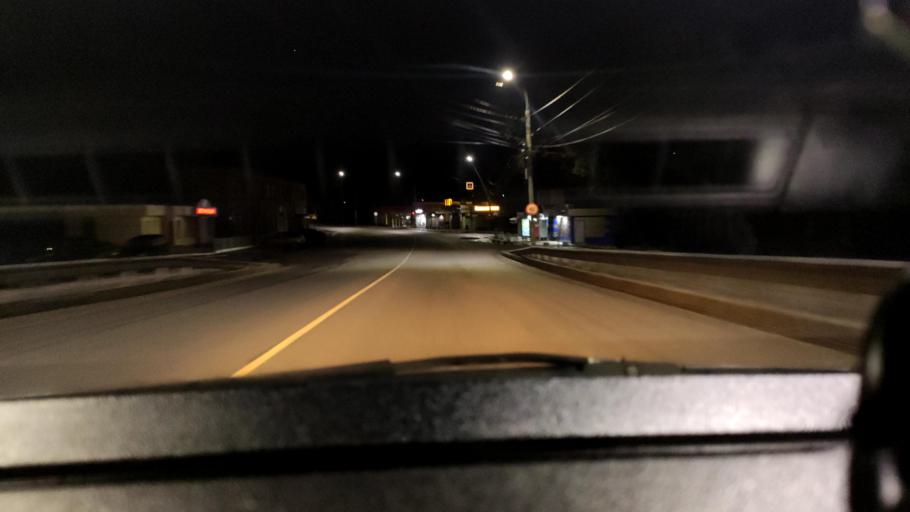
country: RU
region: Voronezj
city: Voronezh
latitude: 51.7248
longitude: 39.2624
